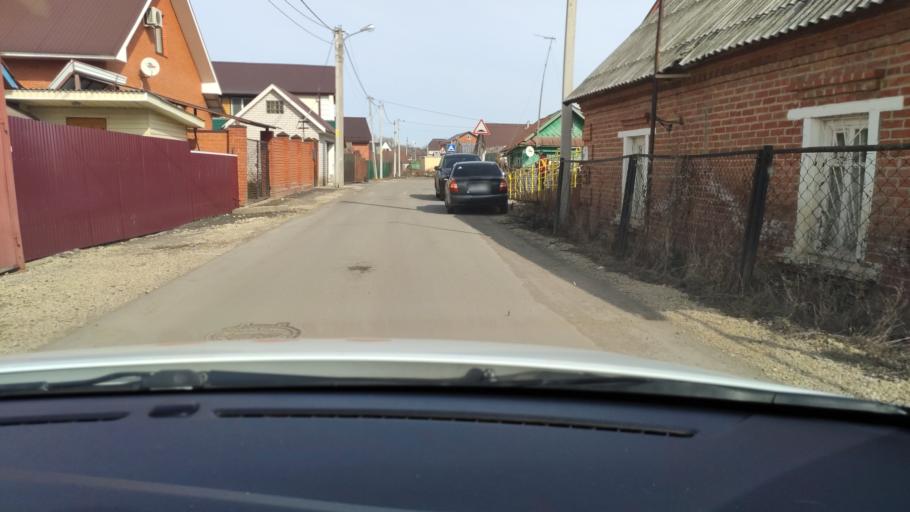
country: RU
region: Tatarstan
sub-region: Gorod Kazan'
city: Kazan
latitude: 55.7254
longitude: 49.1429
